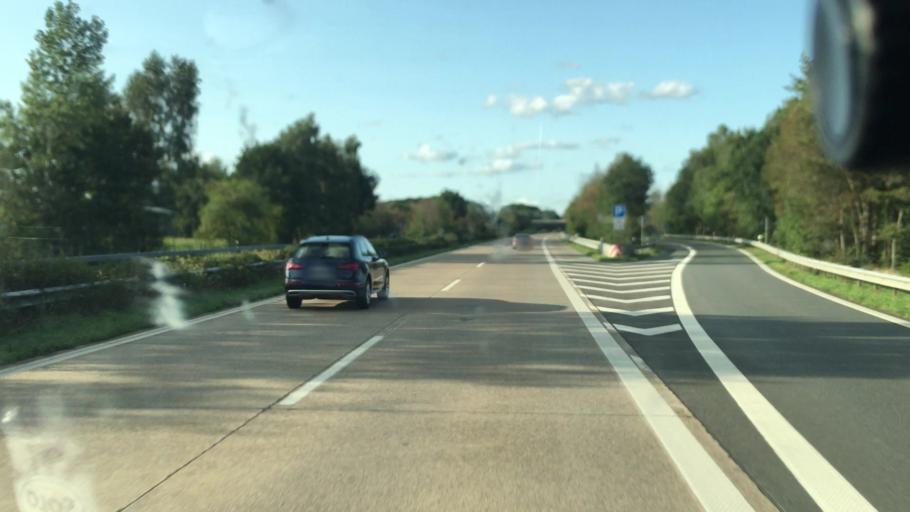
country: DE
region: Lower Saxony
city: Wiefelstede
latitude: 53.2931
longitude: 8.1478
